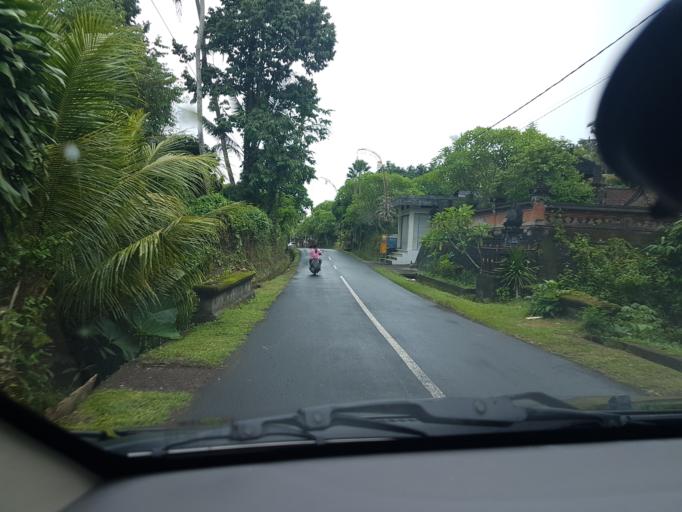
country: ID
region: Bali
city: Banjar Tebongkang
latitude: -8.5312
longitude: 115.2372
